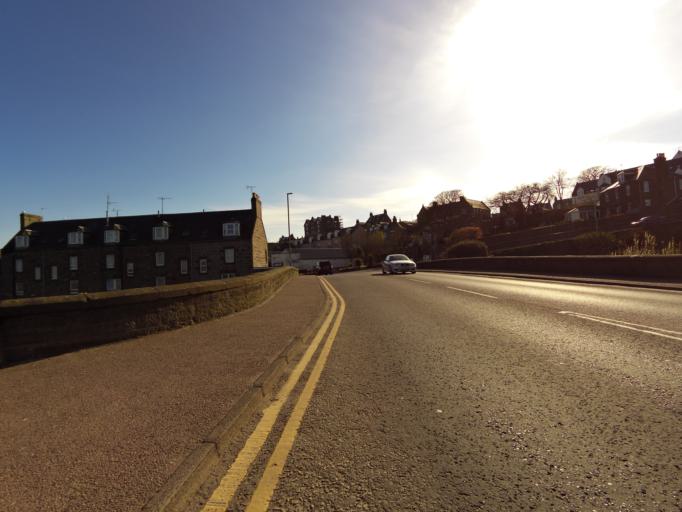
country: GB
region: Scotland
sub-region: Aberdeenshire
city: Stonehaven
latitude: 56.9680
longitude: -2.2090
